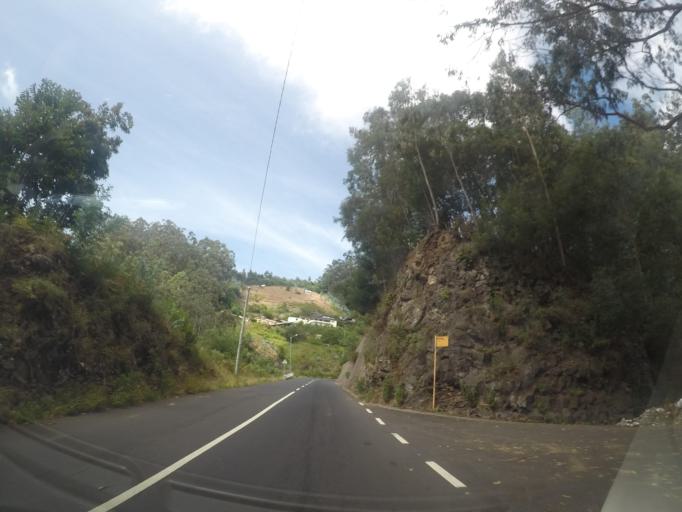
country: PT
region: Madeira
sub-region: Camara de Lobos
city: Curral das Freiras
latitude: 32.6876
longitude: -16.9513
